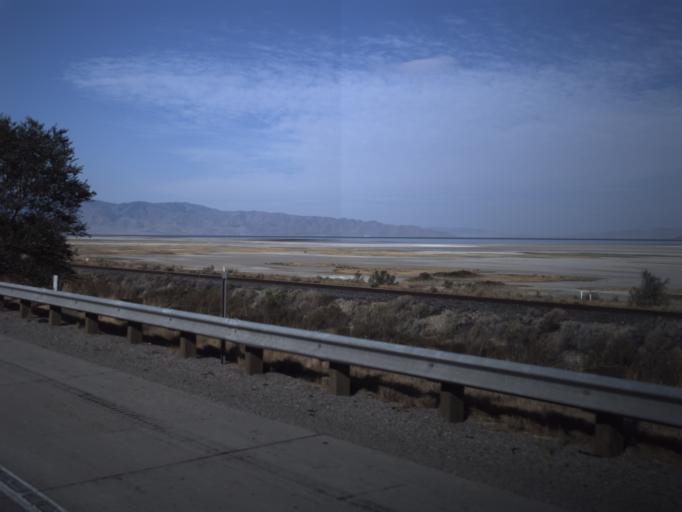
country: US
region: Utah
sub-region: Tooele County
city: Stansbury park
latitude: 40.7080
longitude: -112.2522
